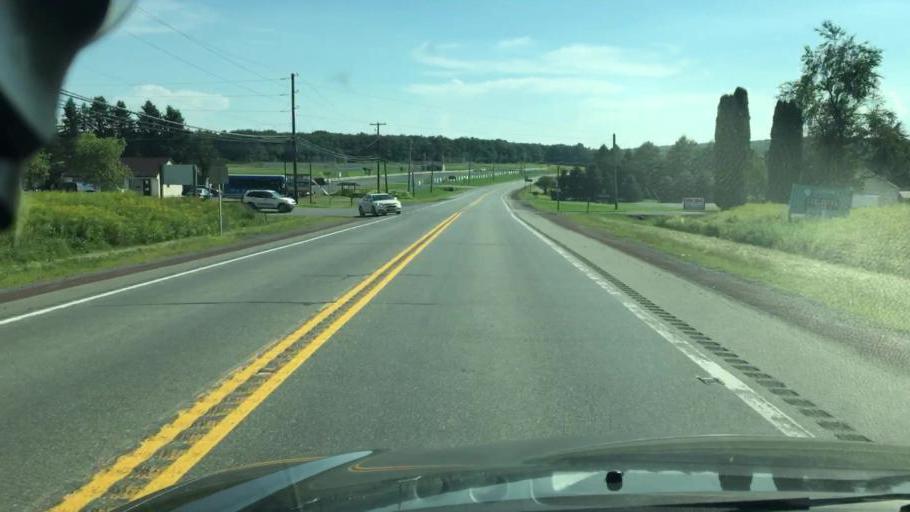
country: US
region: Pennsylvania
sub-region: Carbon County
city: Jim Thorpe
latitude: 40.9356
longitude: -75.6572
